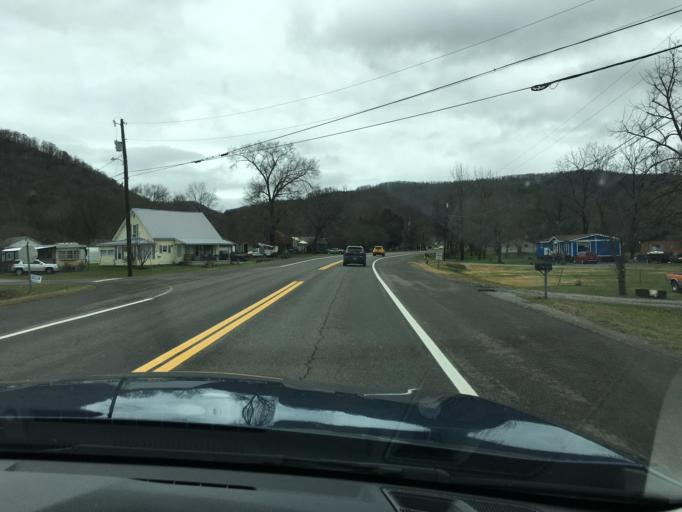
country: US
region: Tennessee
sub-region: Rhea County
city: Spring City
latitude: 35.6989
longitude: -84.8705
